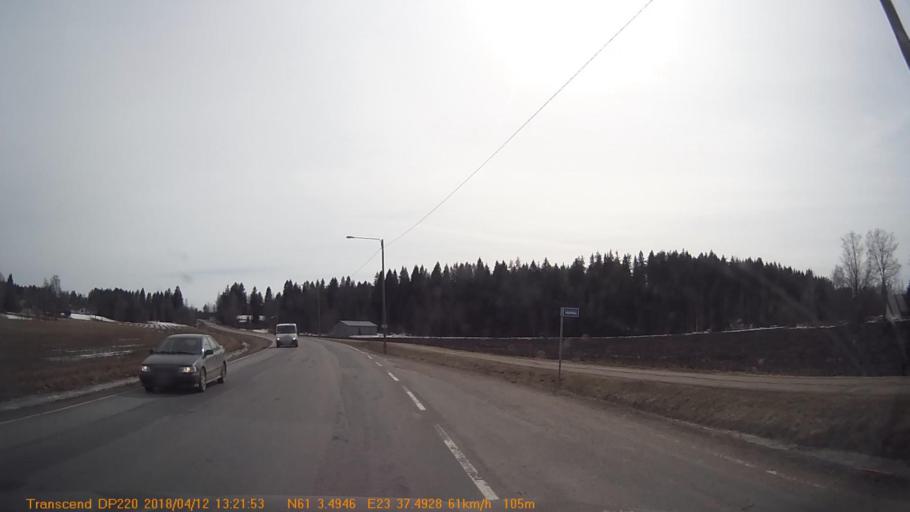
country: FI
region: Pirkanmaa
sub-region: Etelae-Pirkanmaa
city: Urjala
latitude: 61.0571
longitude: 23.6252
